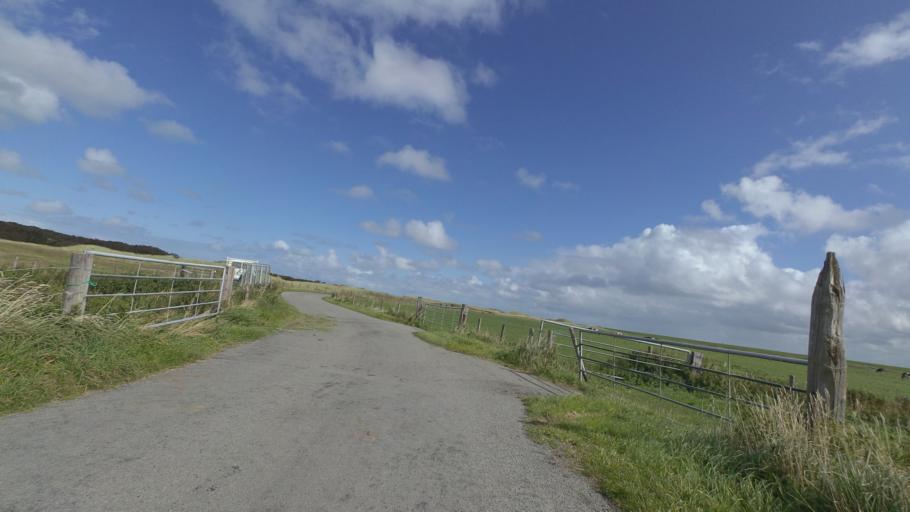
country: NL
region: Friesland
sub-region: Gemeente Ameland
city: Nes
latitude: 53.4482
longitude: 5.8414
